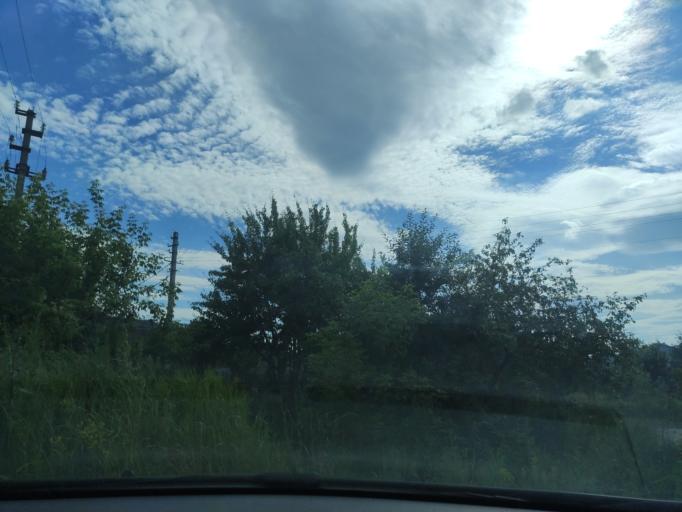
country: RU
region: Ulyanovsk
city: Cherdakly
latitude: 54.4436
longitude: 48.8950
